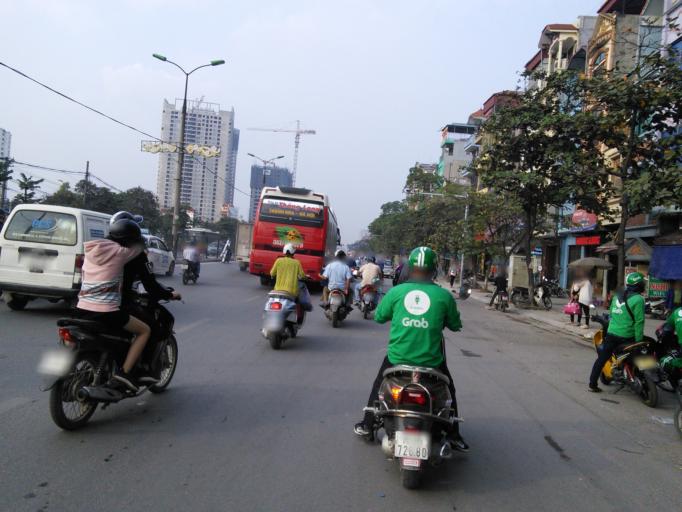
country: VN
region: Ha Noi
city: Hai BaTrung
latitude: 20.9814
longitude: 105.8411
